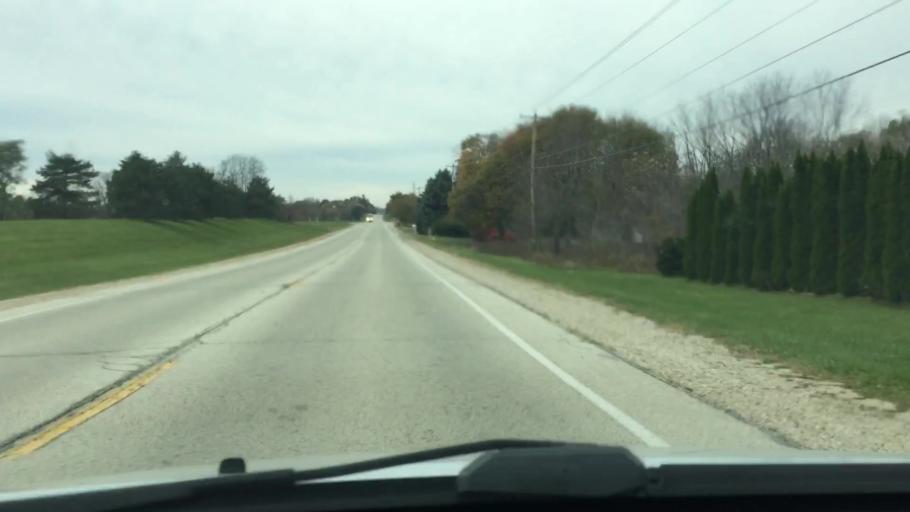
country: US
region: Wisconsin
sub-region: Waukesha County
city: Muskego
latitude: 42.9348
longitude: -88.1765
